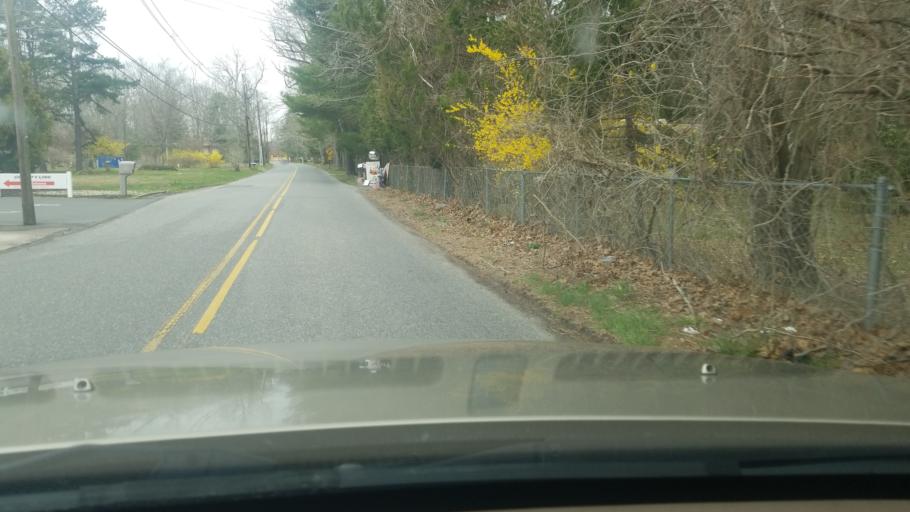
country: US
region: New Jersey
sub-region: Ocean County
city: Lakewood
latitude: 40.1150
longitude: -74.2119
